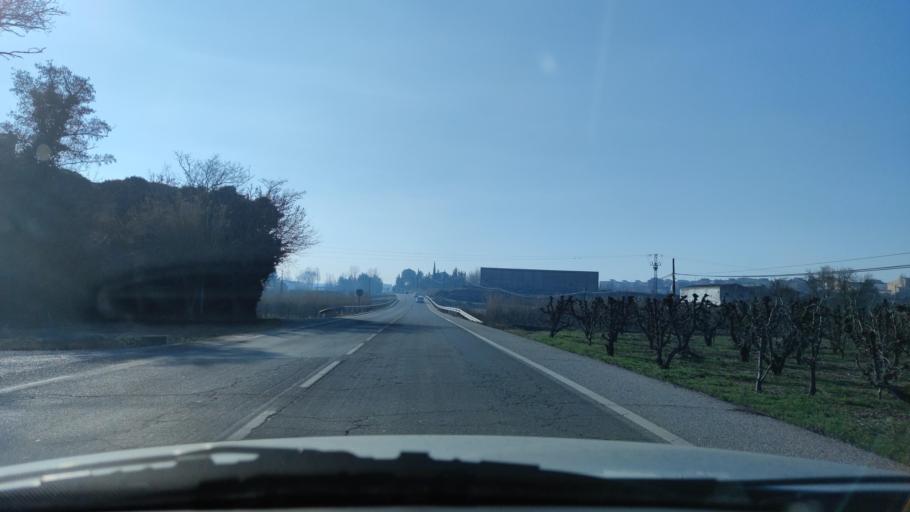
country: ES
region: Catalonia
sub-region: Provincia de Lleida
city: Lleida
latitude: 41.6370
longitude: 0.6365
